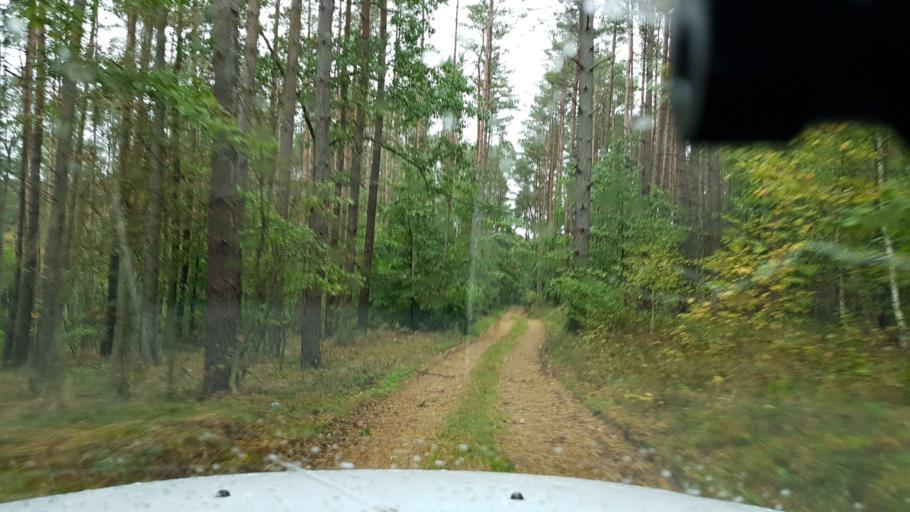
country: PL
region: West Pomeranian Voivodeship
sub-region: Powiat goleniowski
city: Przybiernow
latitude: 53.7384
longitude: 14.7902
